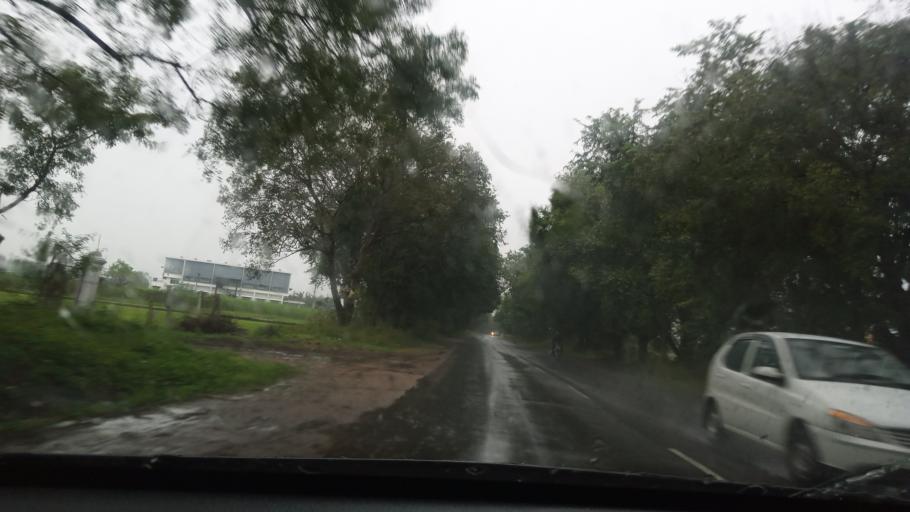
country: IN
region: Tamil Nadu
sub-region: Vellore
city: Kalavai
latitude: 12.8471
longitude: 79.3934
